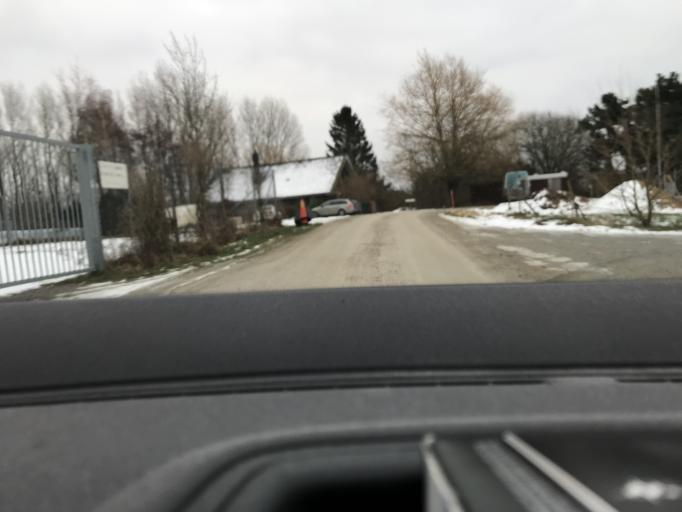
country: SE
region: Skane
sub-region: Ystads Kommun
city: Ystad
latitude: 55.4553
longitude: 13.8587
